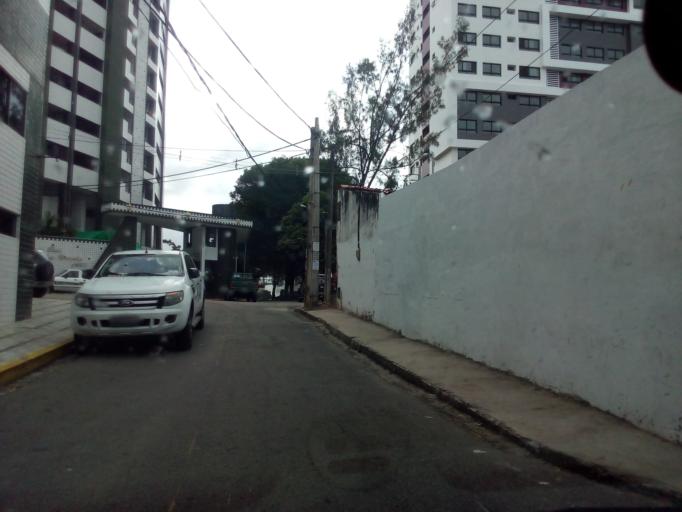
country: BR
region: Rio Grande do Norte
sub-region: Natal
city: Natal
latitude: -5.8012
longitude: -35.2075
